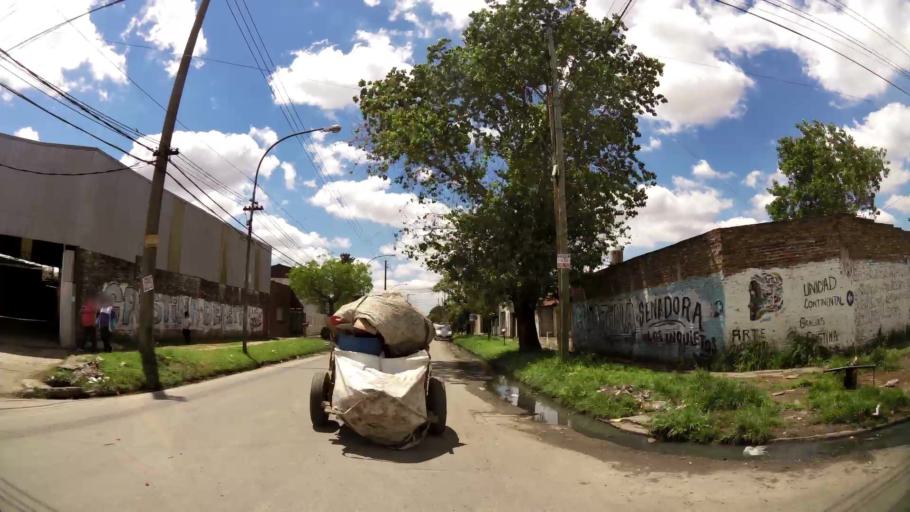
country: AR
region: Buenos Aires
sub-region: Partido de Lanus
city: Lanus
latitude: -34.7036
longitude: -58.4338
